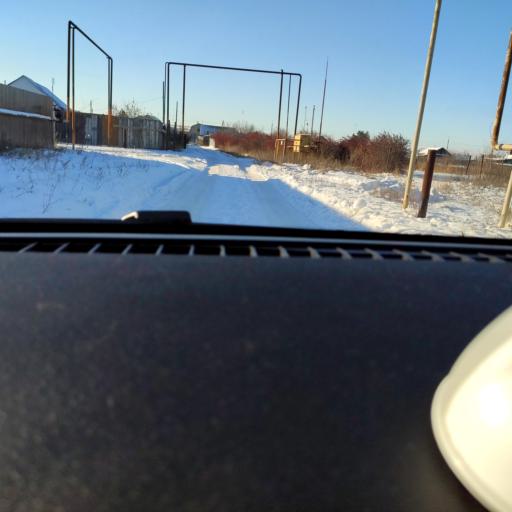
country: RU
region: Samara
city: Spiridonovka
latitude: 53.1033
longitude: 50.6484
